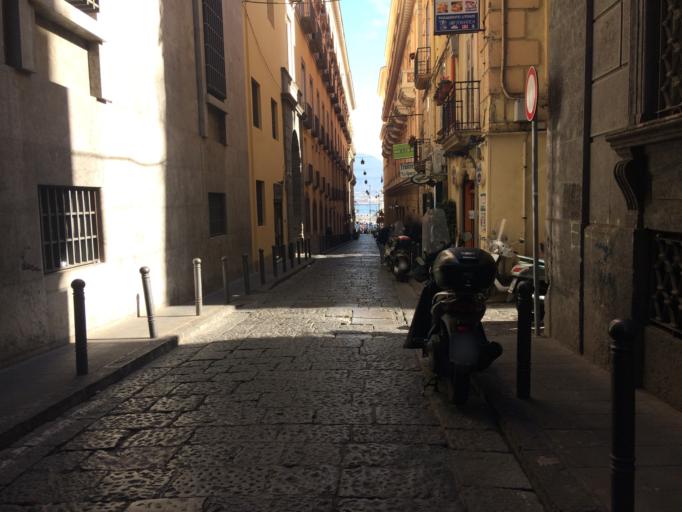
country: IT
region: Campania
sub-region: Provincia di Napoli
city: Napoli
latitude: 40.8400
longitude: 14.2489
